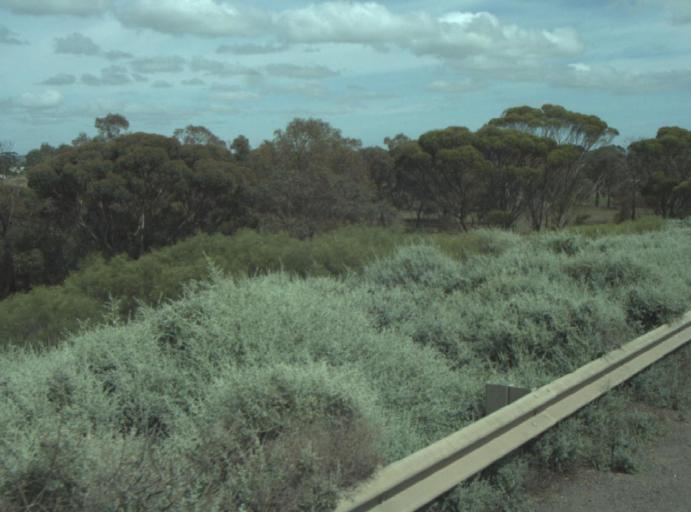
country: AU
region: Victoria
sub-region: Greater Geelong
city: Lara
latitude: -38.0302
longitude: 144.4304
